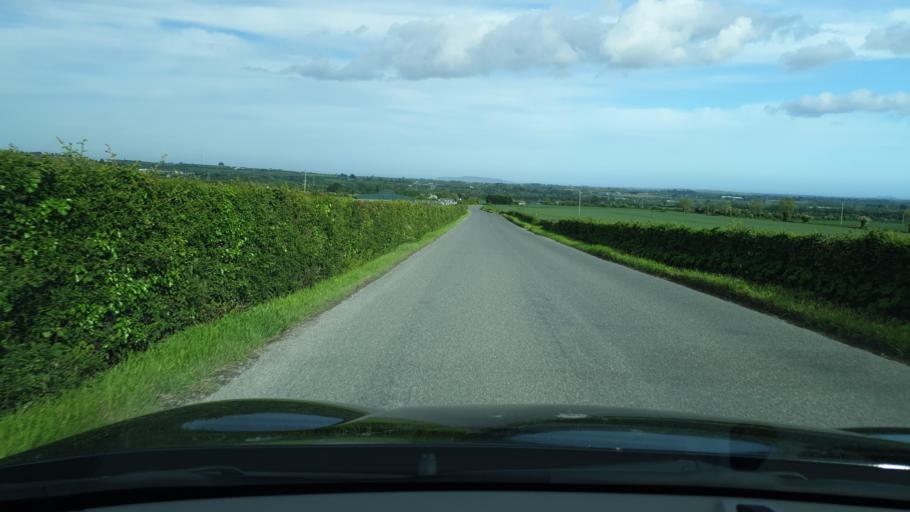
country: IE
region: Leinster
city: Balrothery
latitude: 53.5522
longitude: -6.2364
